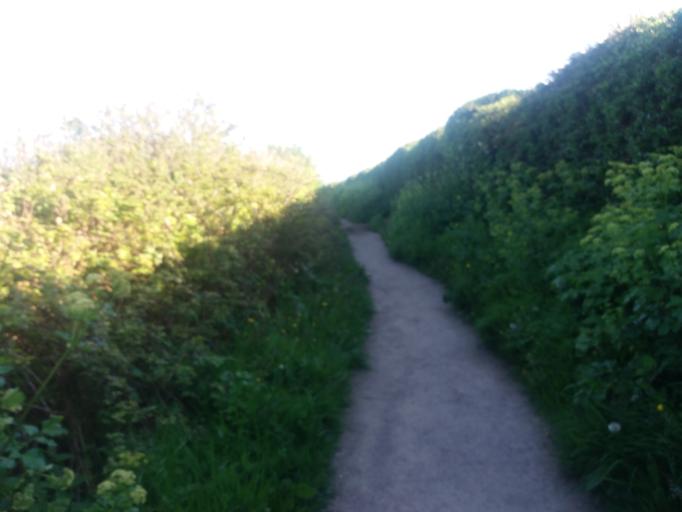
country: IE
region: Leinster
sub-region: Fingal County
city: Howth
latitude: 53.3641
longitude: -6.0723
